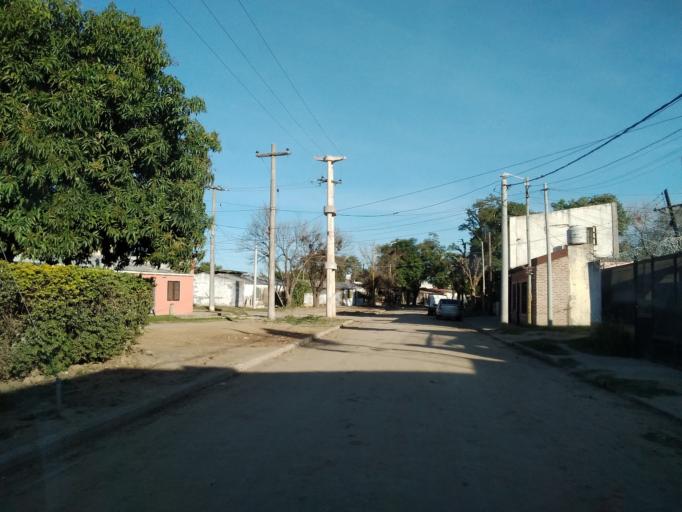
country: AR
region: Corrientes
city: Corrientes
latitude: -27.5022
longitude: -58.8361
